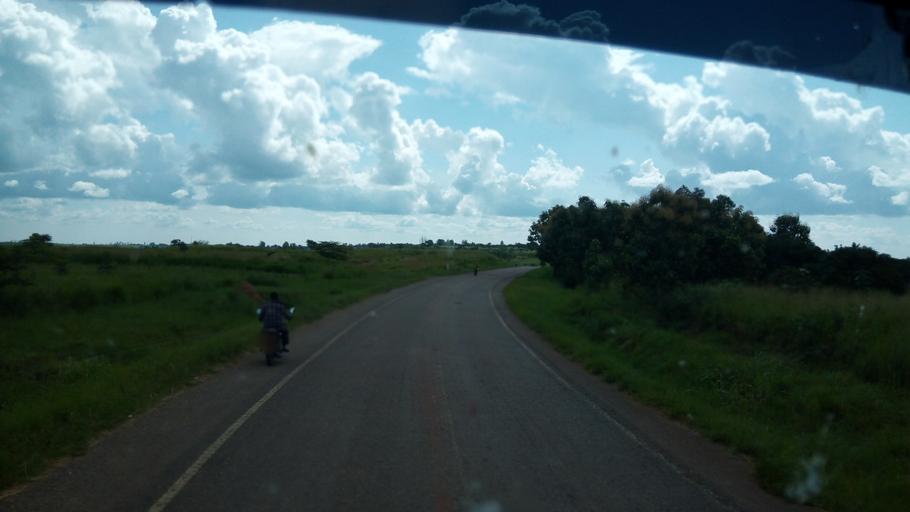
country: UG
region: Northern Region
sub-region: Nwoya District
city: Nwoya
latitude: 2.5383
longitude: 31.8729
